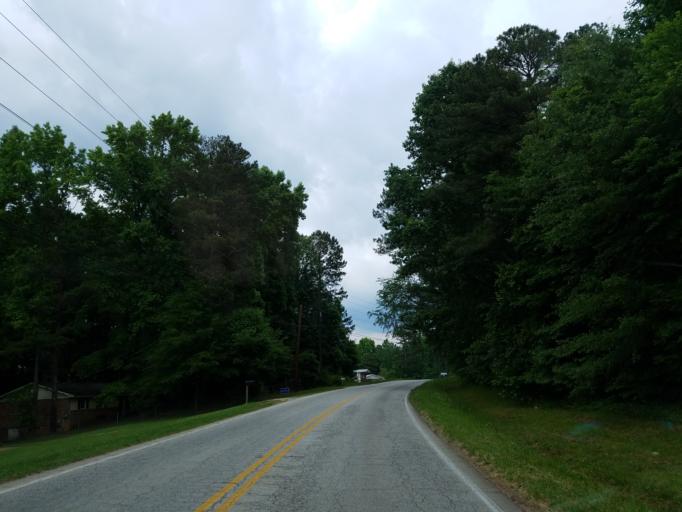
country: US
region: Georgia
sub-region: Douglas County
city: Lithia Springs
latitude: 33.7464
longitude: -84.6622
